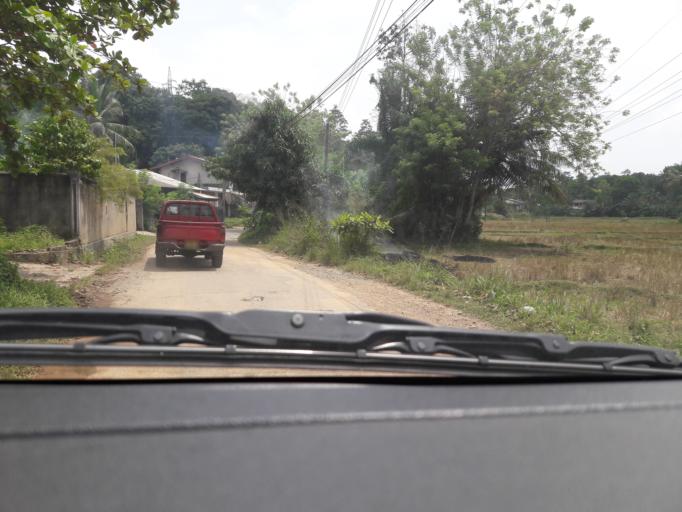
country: LK
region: Southern
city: Unawatuna
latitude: 6.0557
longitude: 80.2491
